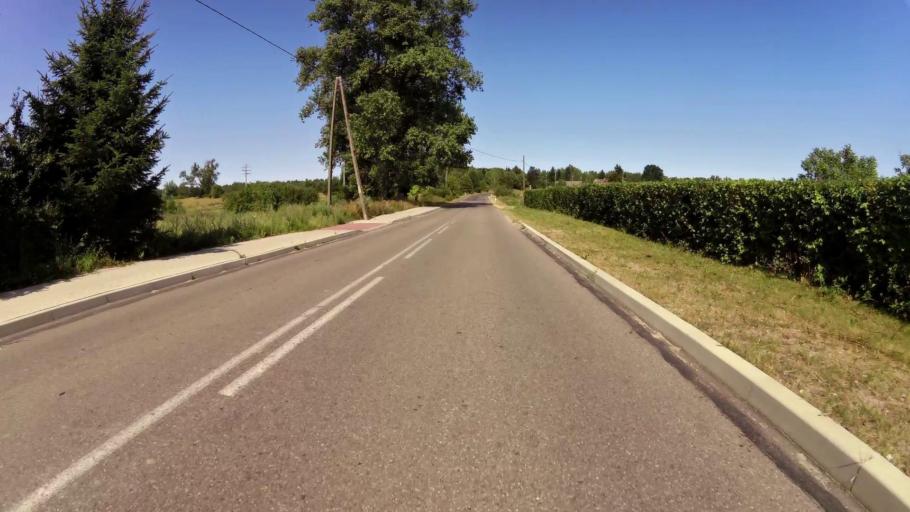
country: PL
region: West Pomeranian Voivodeship
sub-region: Powiat stargardzki
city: Dobrzany
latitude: 53.3465
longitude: 15.3938
